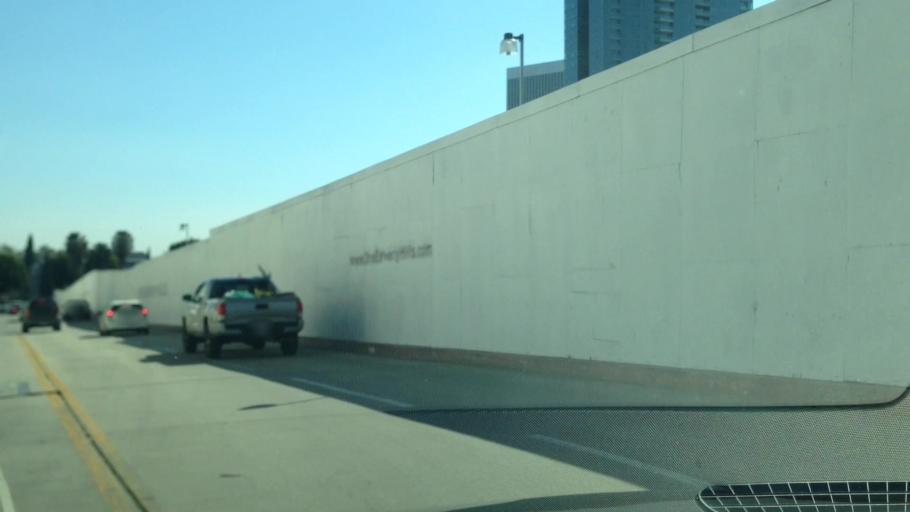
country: US
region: California
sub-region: Los Angeles County
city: Century City
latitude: 34.0665
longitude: -118.4146
